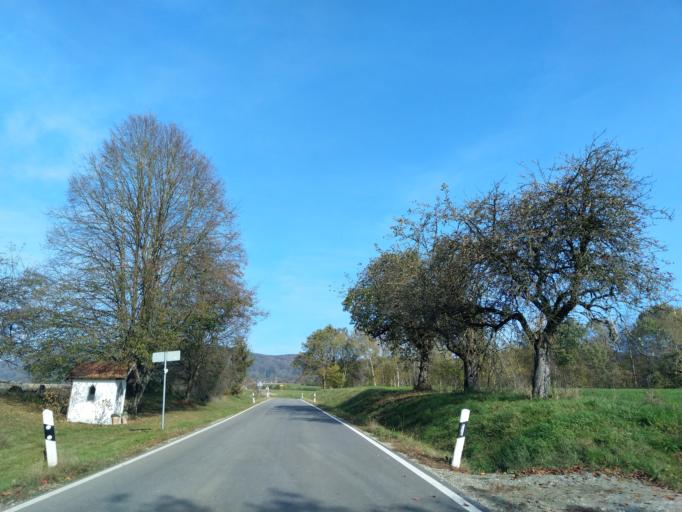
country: DE
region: Bavaria
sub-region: Lower Bavaria
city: Schollnach
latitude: 48.7843
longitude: 13.1804
